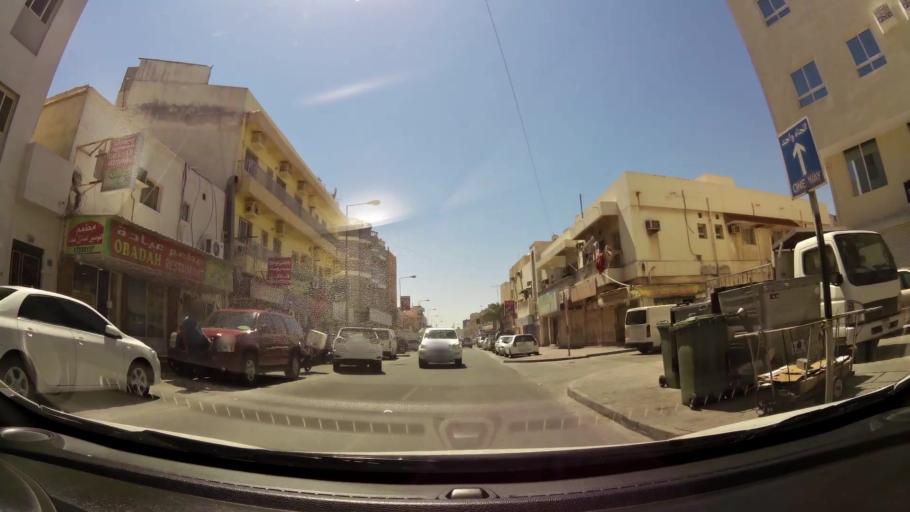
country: BH
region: Muharraq
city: Al Muharraq
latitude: 26.2701
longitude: 50.6092
